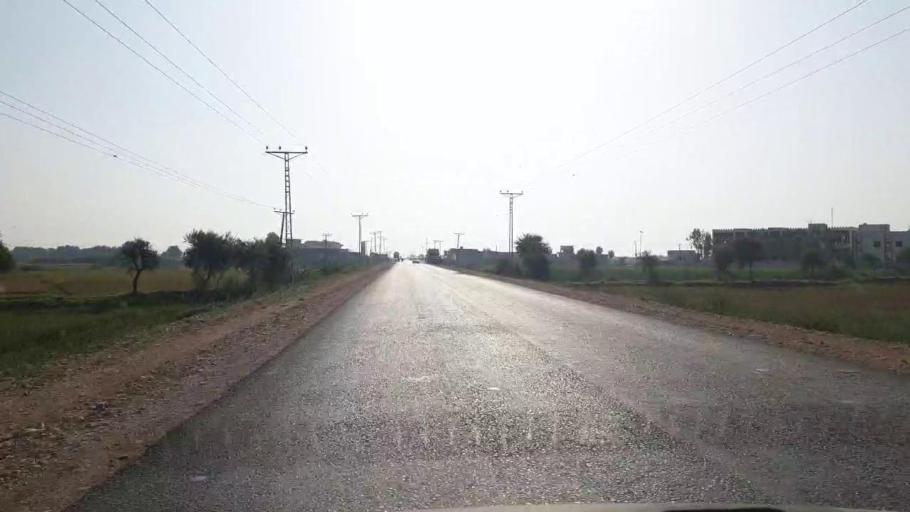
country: PK
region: Sindh
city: Badin
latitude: 24.6676
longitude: 68.8655
